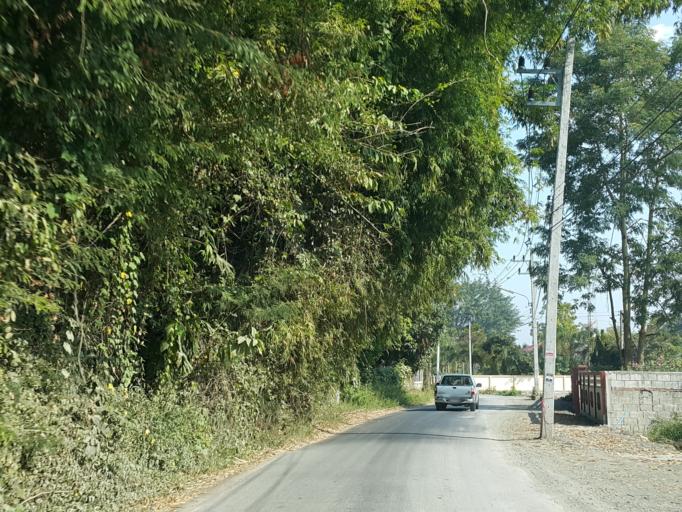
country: TH
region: Chiang Mai
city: San Sai
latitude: 18.8515
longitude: 99.0996
